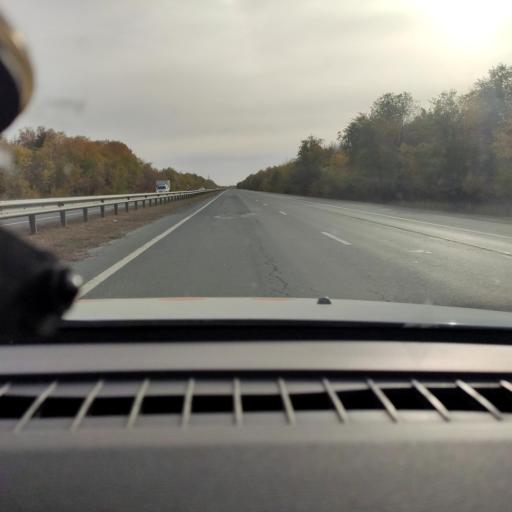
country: RU
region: Samara
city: Novokuybyshevsk
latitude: 53.0382
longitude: 50.0002
